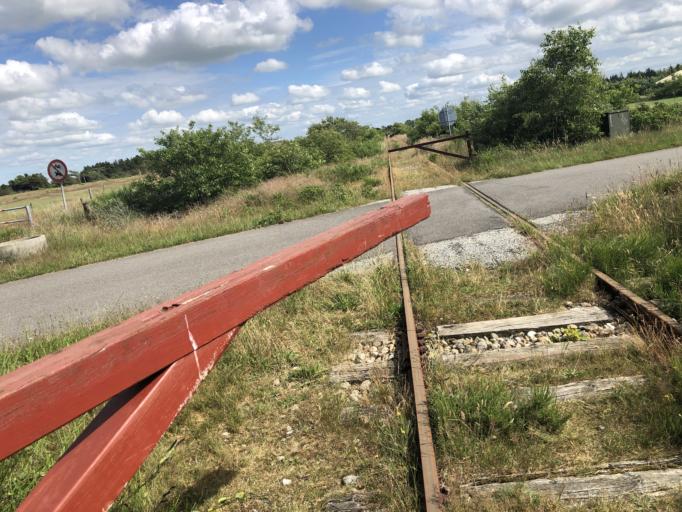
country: DK
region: South Denmark
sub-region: Varde Kommune
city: Oksbol
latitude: 55.8072
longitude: 8.2131
